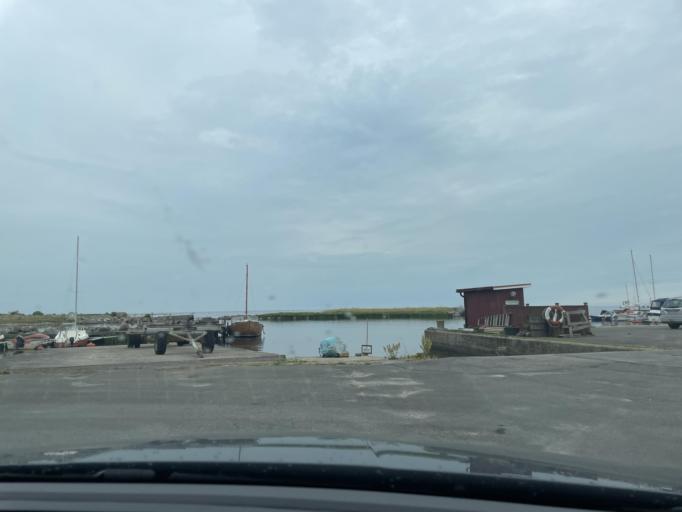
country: SE
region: Skane
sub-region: Bromolla Kommun
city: Bromoella
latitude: 55.9972
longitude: 14.4455
